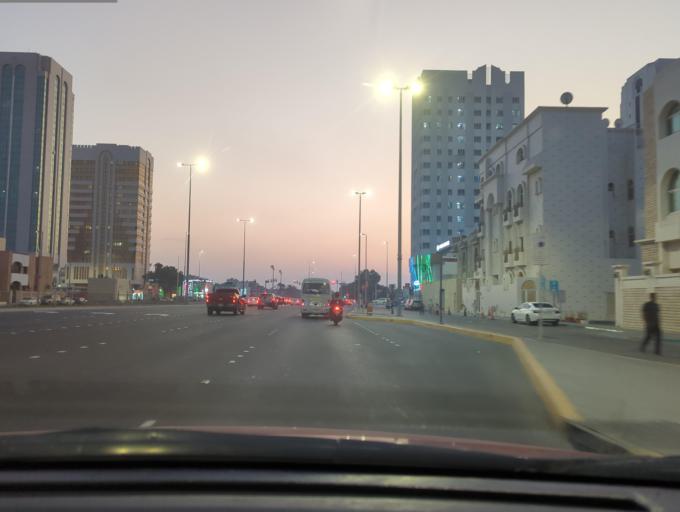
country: AE
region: Abu Dhabi
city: Abu Dhabi
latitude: 24.4644
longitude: 54.3789
